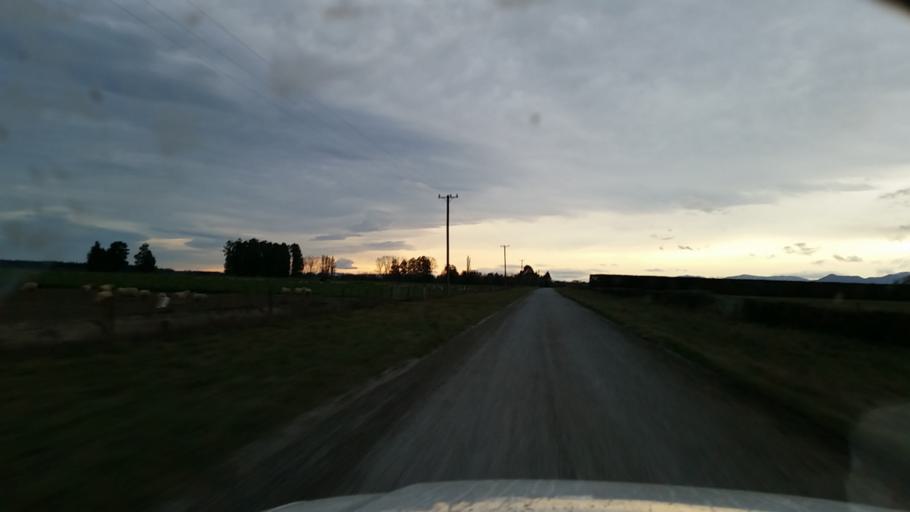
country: NZ
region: Canterbury
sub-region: Ashburton District
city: Ashburton
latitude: -43.8286
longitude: 171.6340
